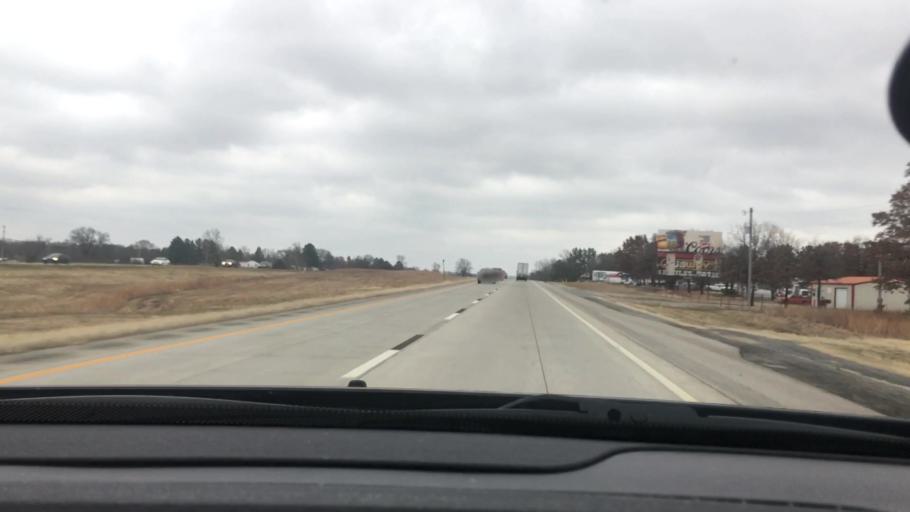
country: US
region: Oklahoma
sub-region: Atoka County
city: Atoka
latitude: 34.2027
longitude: -96.2369
